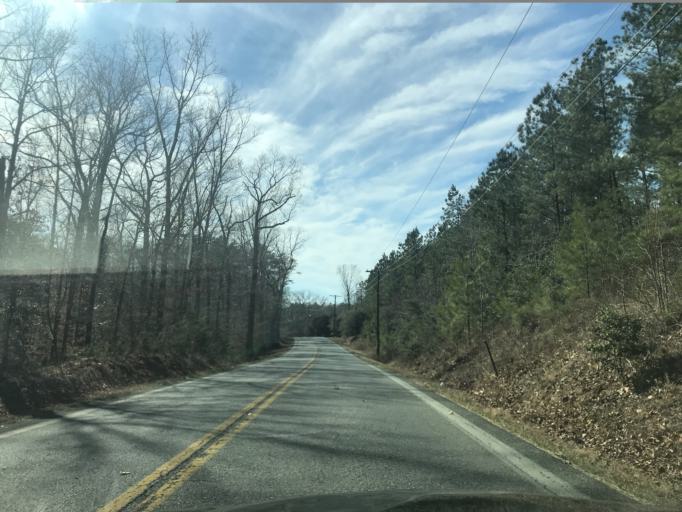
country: US
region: Maryland
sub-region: Charles County
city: Indian Head
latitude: 38.4716
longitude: -77.1590
